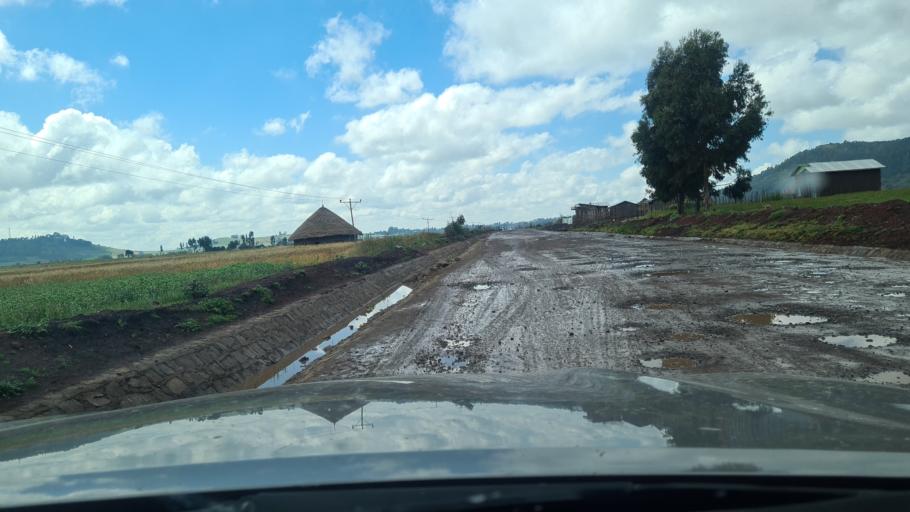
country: ET
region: Oromiya
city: Huruta
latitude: 8.0864
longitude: 39.5407
